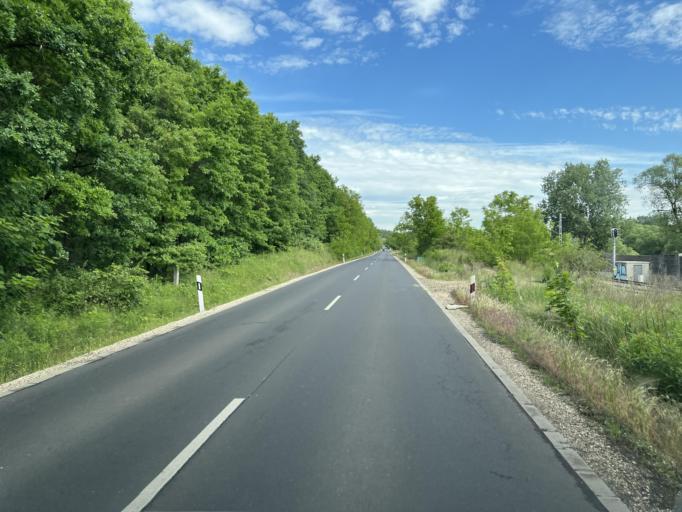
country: HU
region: Pest
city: Pecel
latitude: 47.5122
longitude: 19.3694
